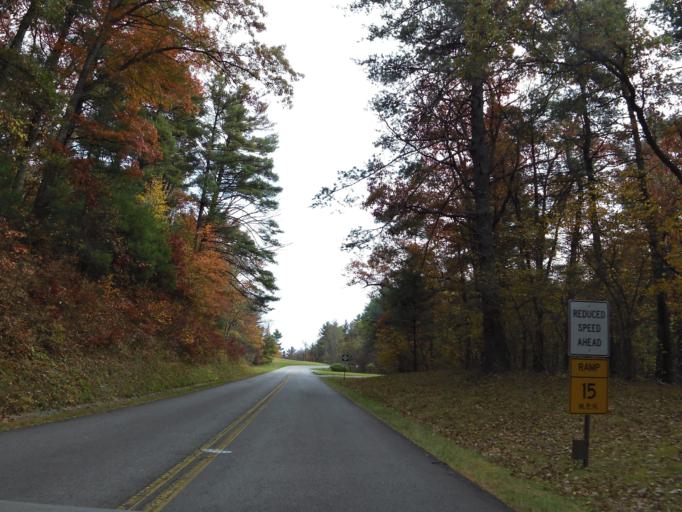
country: US
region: Virginia
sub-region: City of Galax
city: Galax
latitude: 36.5586
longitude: -80.9100
